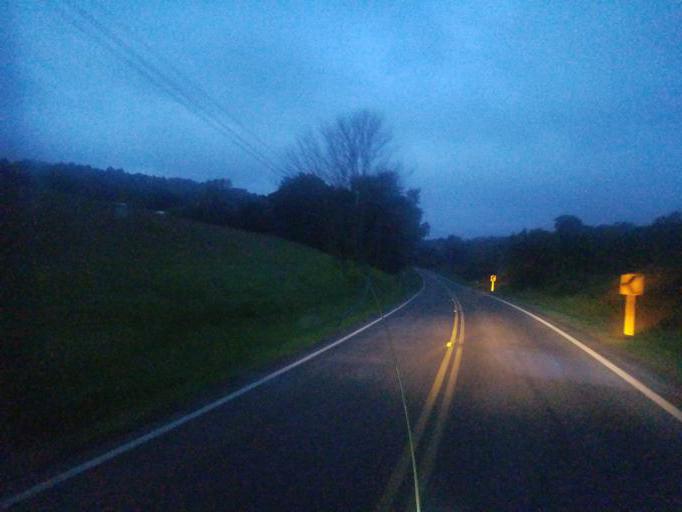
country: US
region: Ohio
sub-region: Carroll County
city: Carrollton
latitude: 40.5798
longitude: -81.0385
